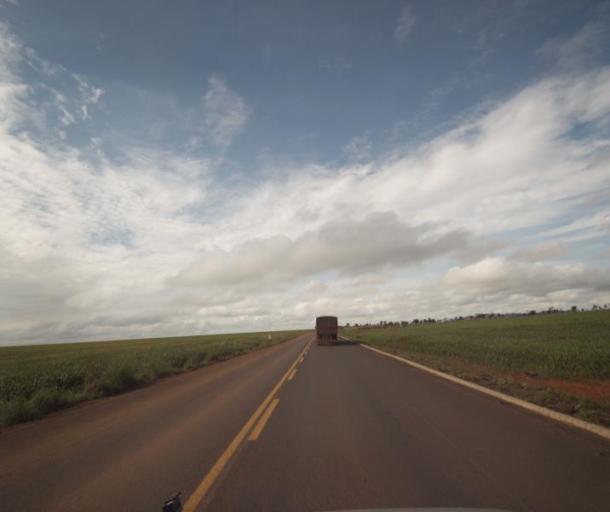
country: BR
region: Goias
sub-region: Padre Bernardo
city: Padre Bernardo
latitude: -15.4184
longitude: -48.6241
